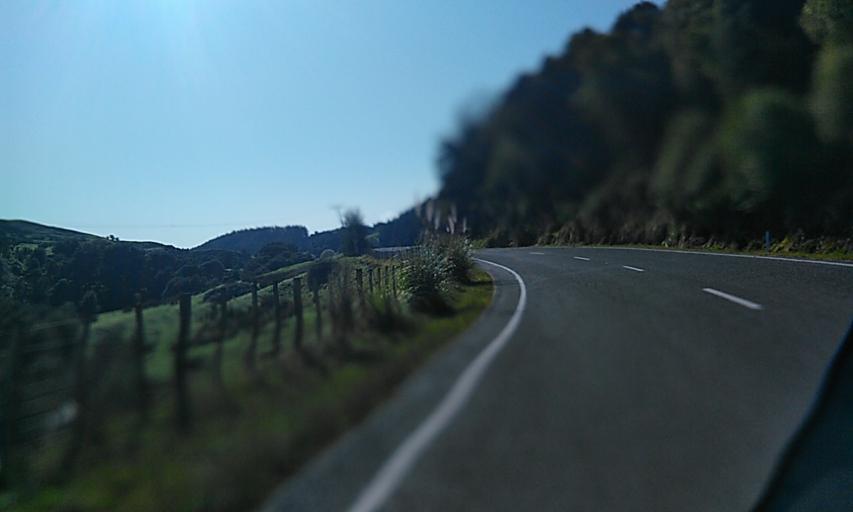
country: NZ
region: Gisborne
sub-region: Gisborne District
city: Gisborne
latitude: -38.5845
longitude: 178.0032
